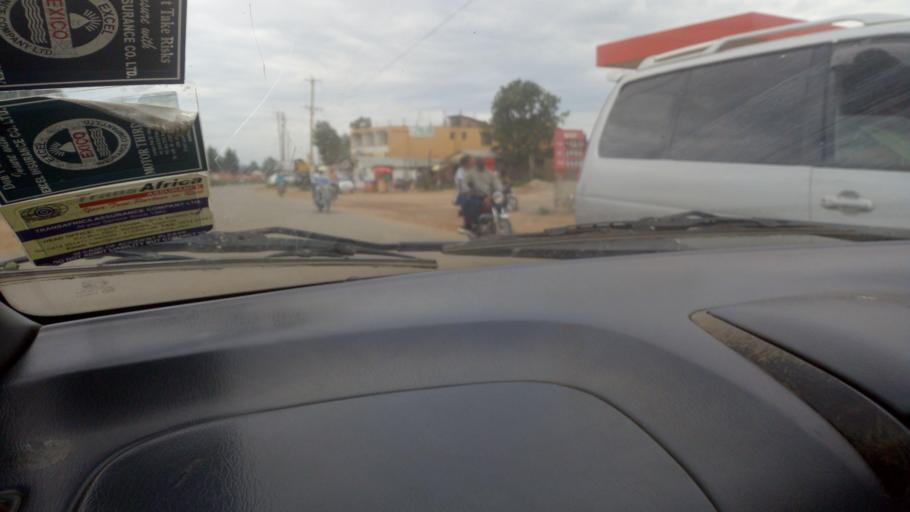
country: UG
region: Western Region
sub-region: Mbarara District
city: Mbarara
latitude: -0.6041
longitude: 30.6476
